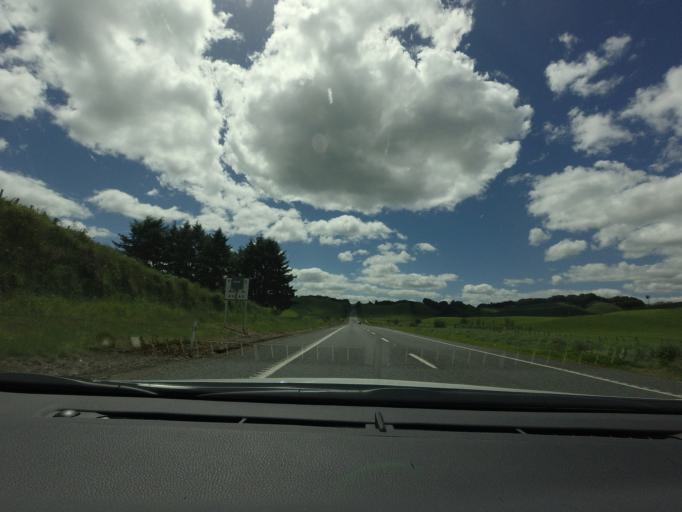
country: NZ
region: Bay of Plenty
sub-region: Rotorua District
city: Rotorua
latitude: -38.2592
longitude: 176.3198
